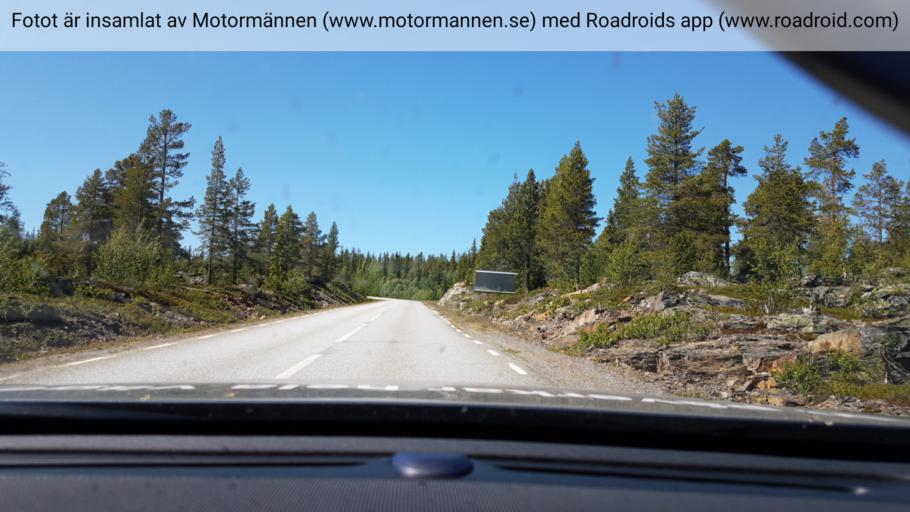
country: SE
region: Vaesterbotten
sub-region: Vilhelmina Kommun
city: Sjoberg
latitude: 64.9565
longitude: 15.4618
